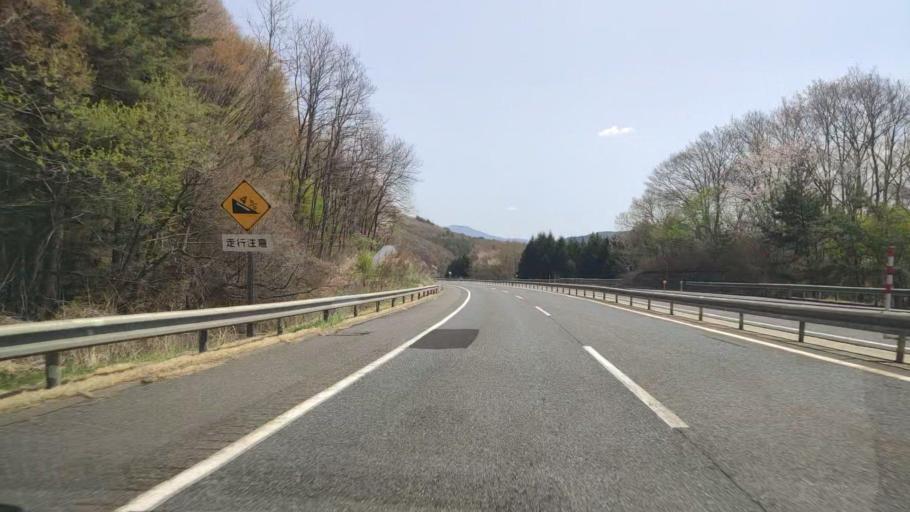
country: JP
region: Iwate
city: Ichinohe
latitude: 40.2181
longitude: 141.2337
